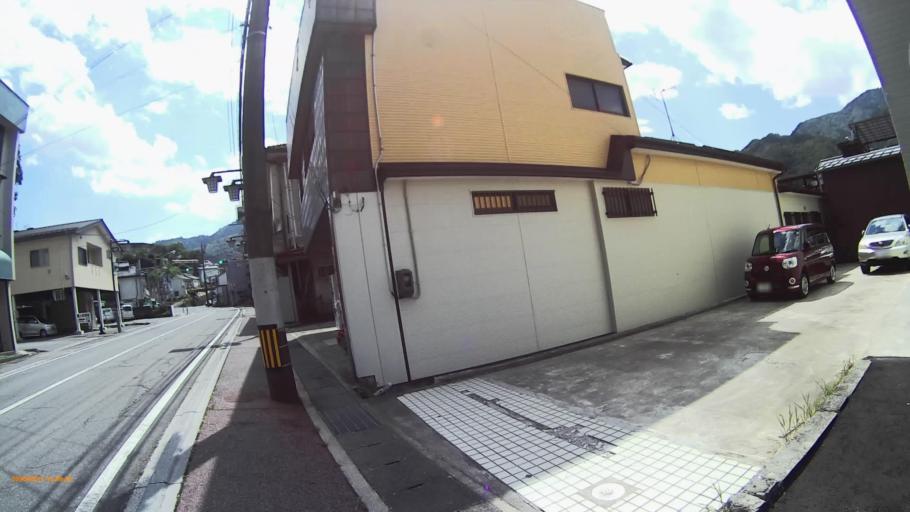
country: JP
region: Nagano
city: Ina
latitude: 35.7833
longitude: 137.6947
